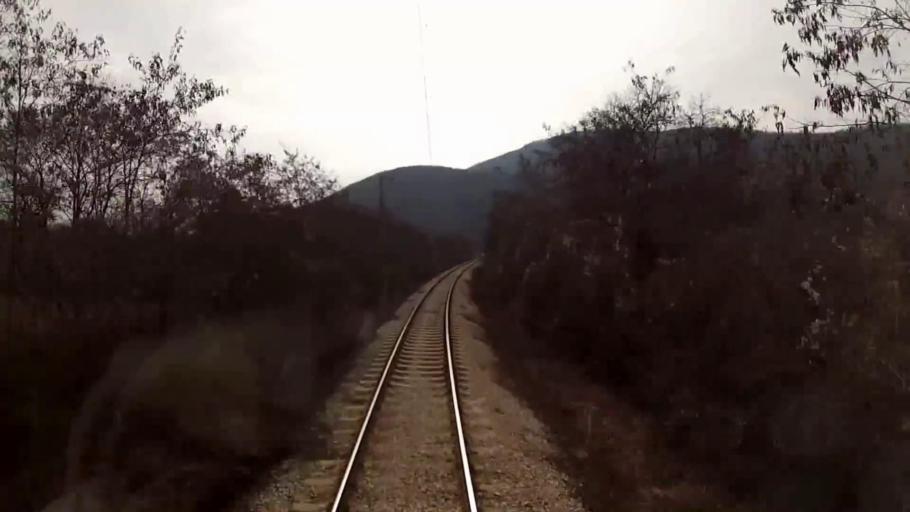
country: BG
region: Sofiya
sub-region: Obshtina Gorna Malina
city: Gorna Malina
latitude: 42.6901
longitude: 23.8018
